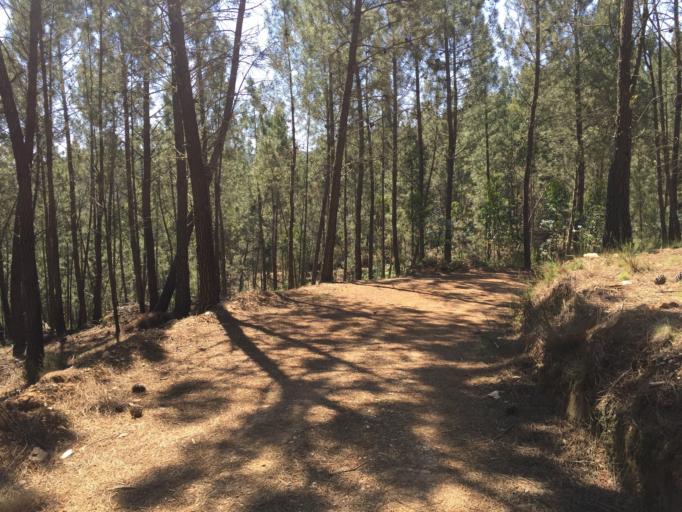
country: PT
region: Coimbra
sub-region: Pampilhosa da Serra
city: Pampilhosa da Serra
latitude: 40.0762
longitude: -7.7790
